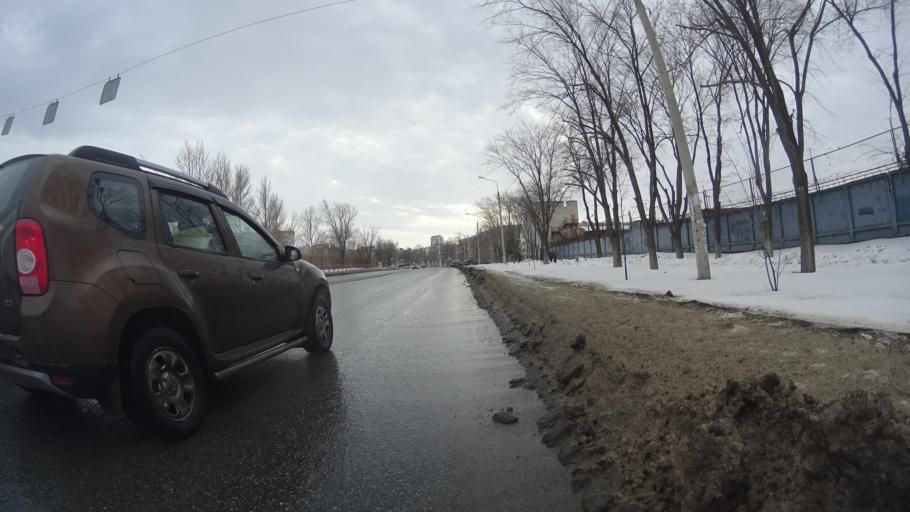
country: RU
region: Chelyabinsk
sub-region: Gorod Chelyabinsk
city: Chelyabinsk
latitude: 55.2032
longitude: 61.3232
